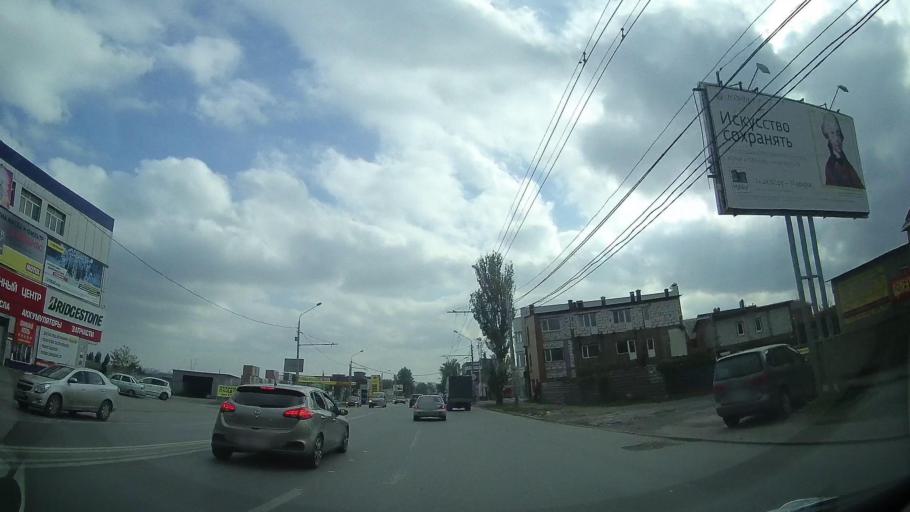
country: RU
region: Rostov
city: Severnyy
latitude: 47.2804
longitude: 39.6836
